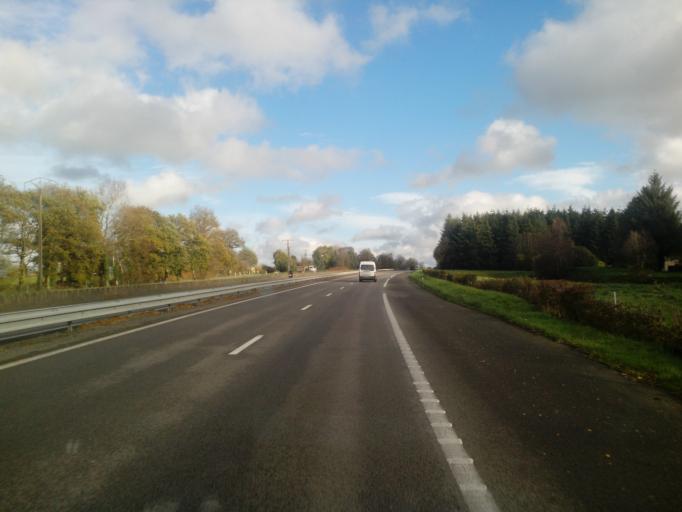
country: FR
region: Brittany
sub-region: Departement du Morbihan
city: Plumelin
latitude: 47.8954
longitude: -2.9145
